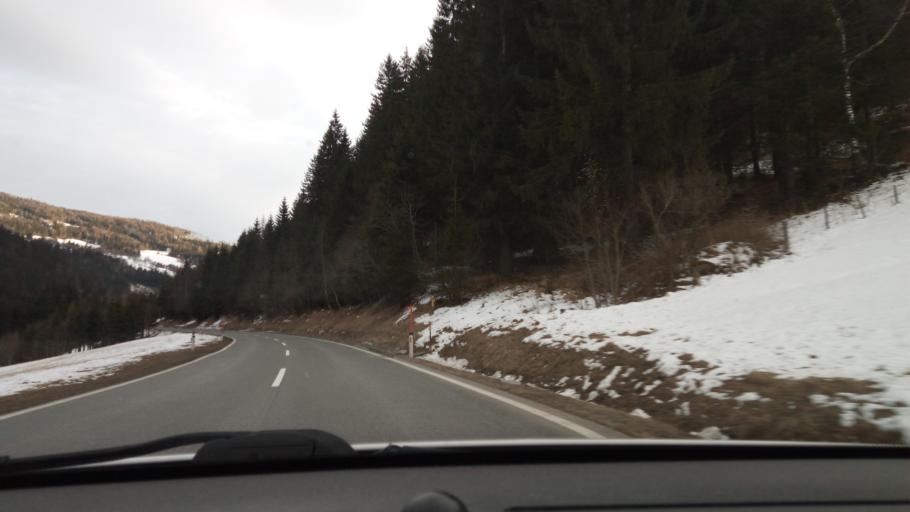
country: AT
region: Salzburg
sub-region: Politischer Bezirk Tamsweg
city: Tamsweg
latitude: 47.1105
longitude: 13.8155
